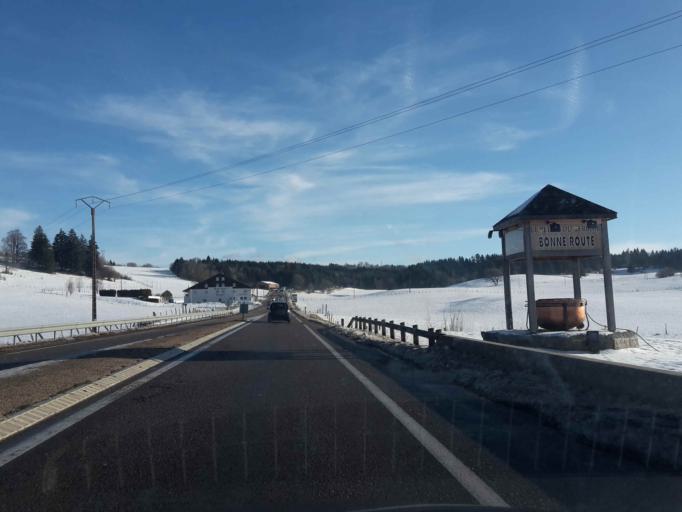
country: FR
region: Franche-Comte
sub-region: Departement du Doubs
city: Doubs
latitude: 46.9786
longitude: 6.3388
